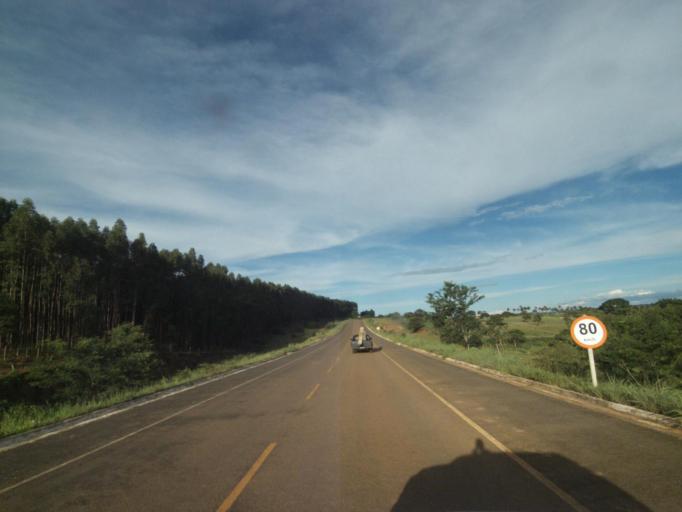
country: BR
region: Goias
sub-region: Jaragua
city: Jaragua
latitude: -15.8839
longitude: -49.4473
